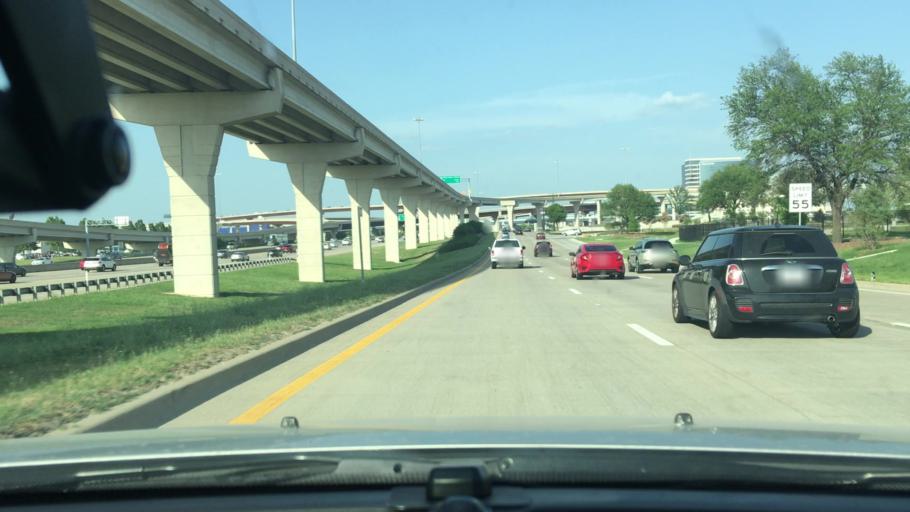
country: US
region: Texas
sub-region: Denton County
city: The Colony
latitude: 33.0885
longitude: -96.8300
